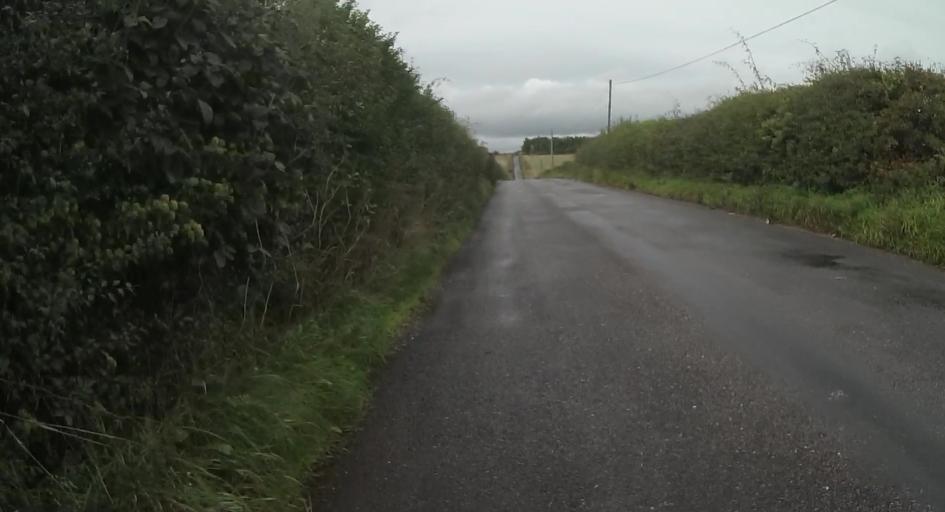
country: GB
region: England
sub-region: Hampshire
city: Tadley
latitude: 51.2892
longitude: -1.1449
